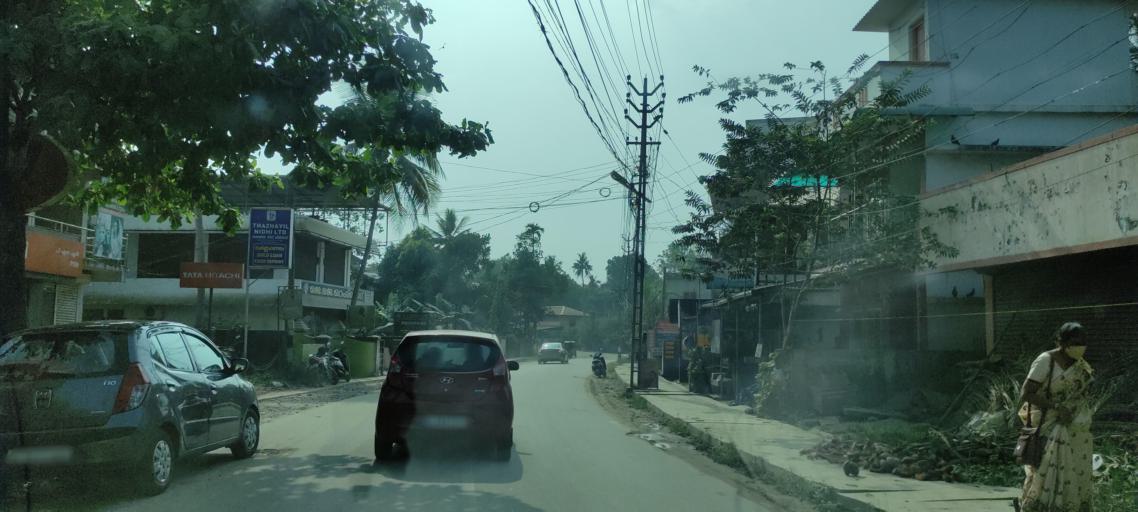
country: IN
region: Kerala
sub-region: Pattanamtitta
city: Tiruvalla
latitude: 9.3772
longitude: 76.5570
